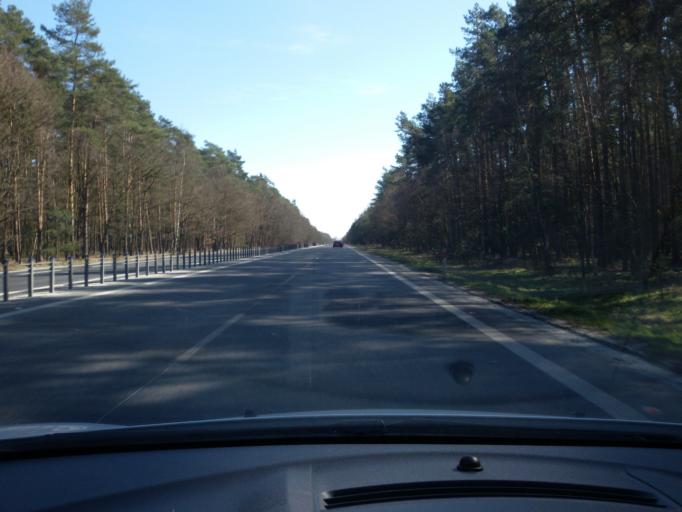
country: PL
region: Greater Poland Voivodeship
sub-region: Powiat leszczynski
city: Rydzyna
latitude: 51.8121
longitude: 16.6289
